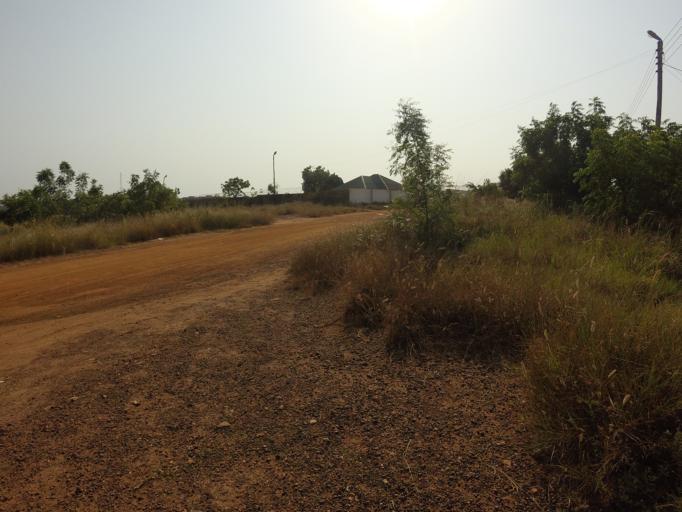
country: GH
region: Greater Accra
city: Tema
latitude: 5.7050
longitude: 0.0605
